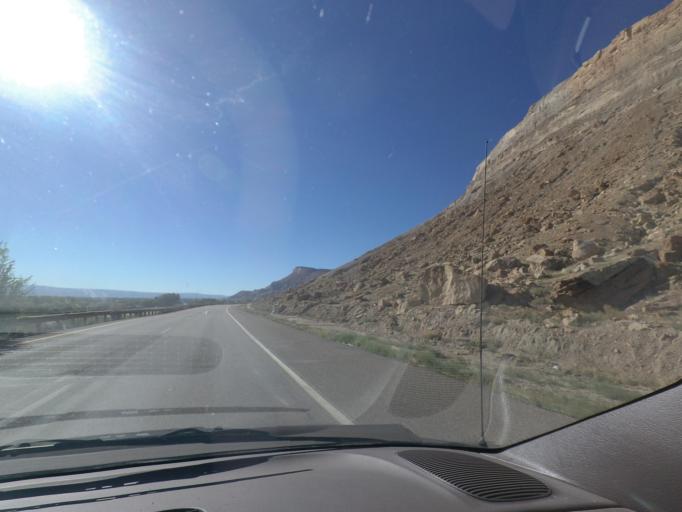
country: US
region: Colorado
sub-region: Mesa County
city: Palisade
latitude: 39.1177
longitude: -108.3511
